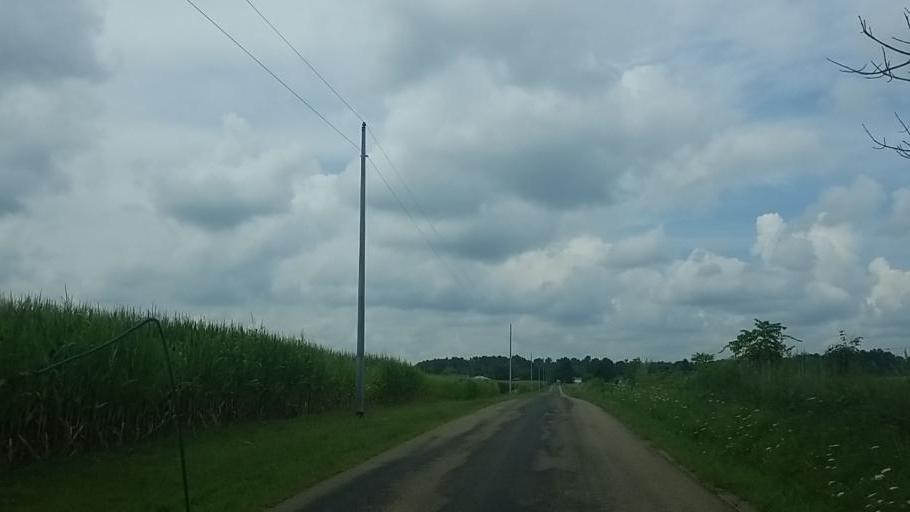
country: US
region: Ohio
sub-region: Knox County
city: Gambier
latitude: 40.3346
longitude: -82.4312
